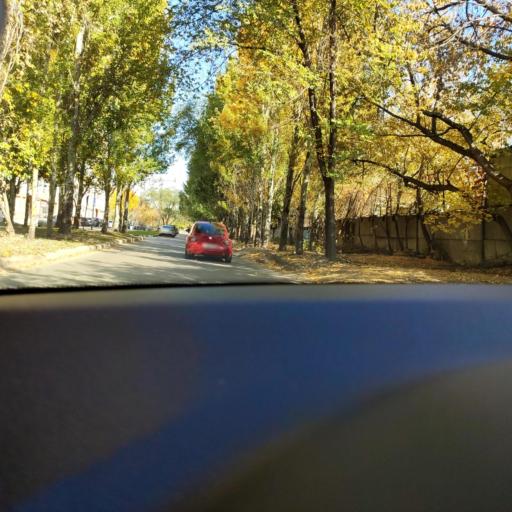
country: RU
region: Samara
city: Samara
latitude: 53.2432
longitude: 50.2035
